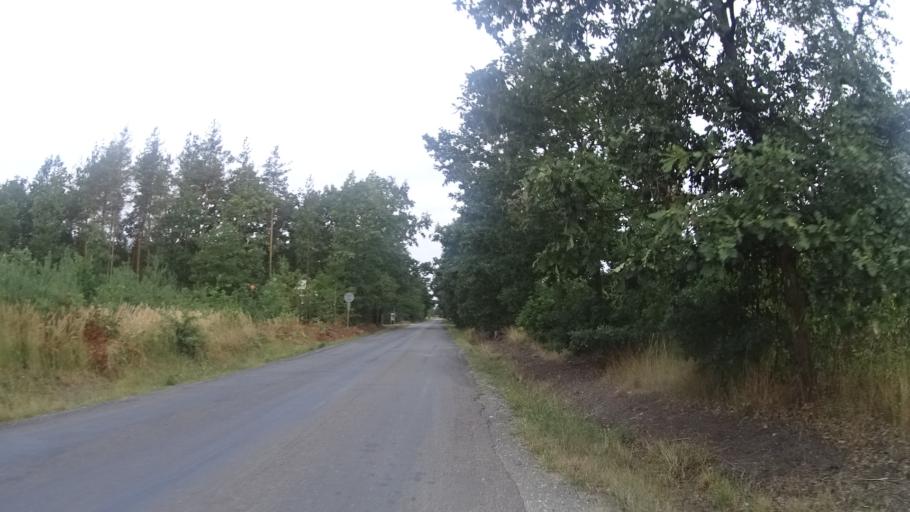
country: CZ
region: Kralovehradecky
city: Cernilov
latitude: 50.2052
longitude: 15.9273
